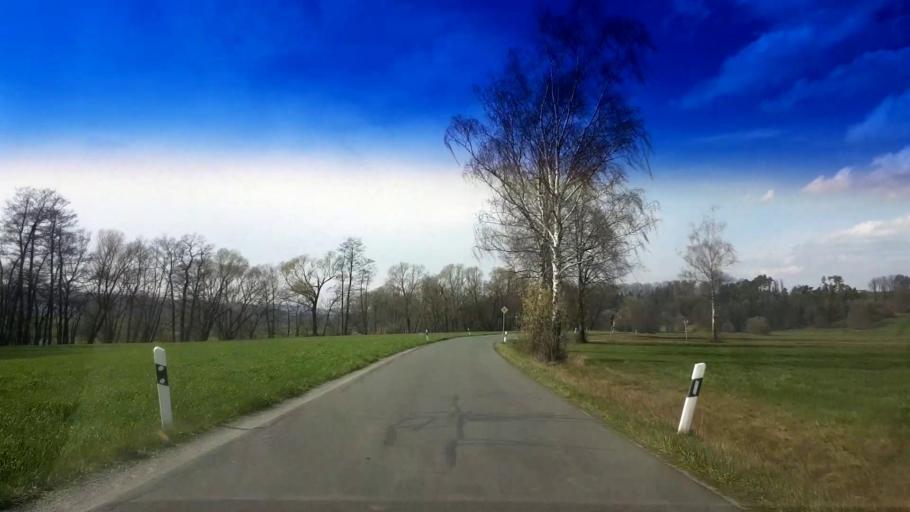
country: DE
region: Bavaria
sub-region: Upper Franconia
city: Gesees
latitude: 50.0278
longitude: 11.6412
